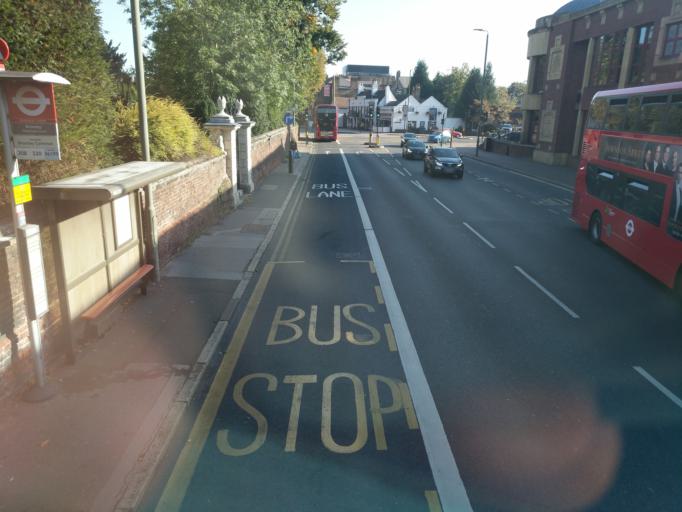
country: GB
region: England
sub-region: Greater London
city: Bromley
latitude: 51.4079
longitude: 0.0113
